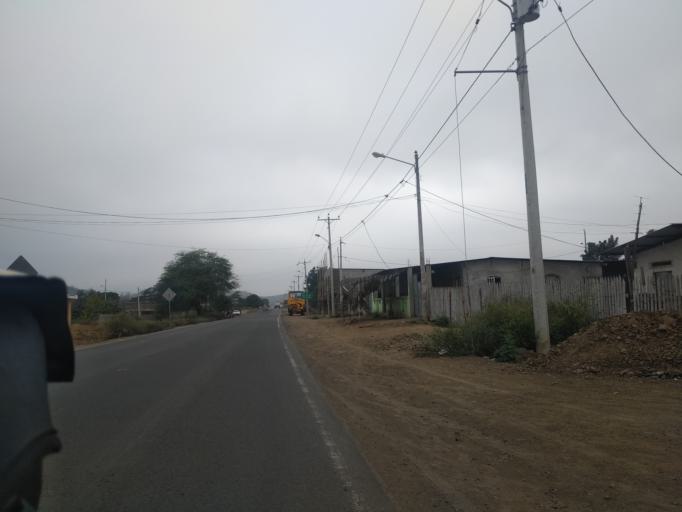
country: EC
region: Manabi
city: Montecristi
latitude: -1.0807
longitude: -80.6742
